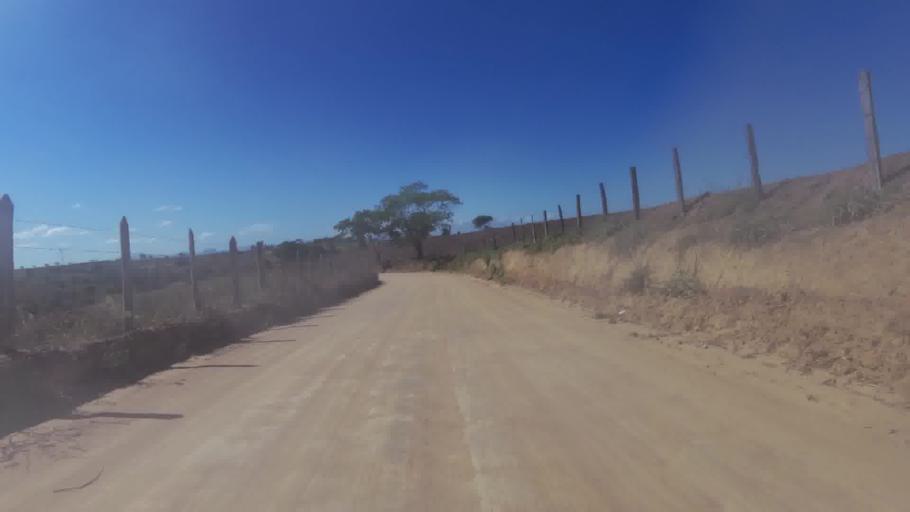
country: BR
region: Espirito Santo
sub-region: Marataizes
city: Marataizes
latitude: -21.1535
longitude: -40.9830
